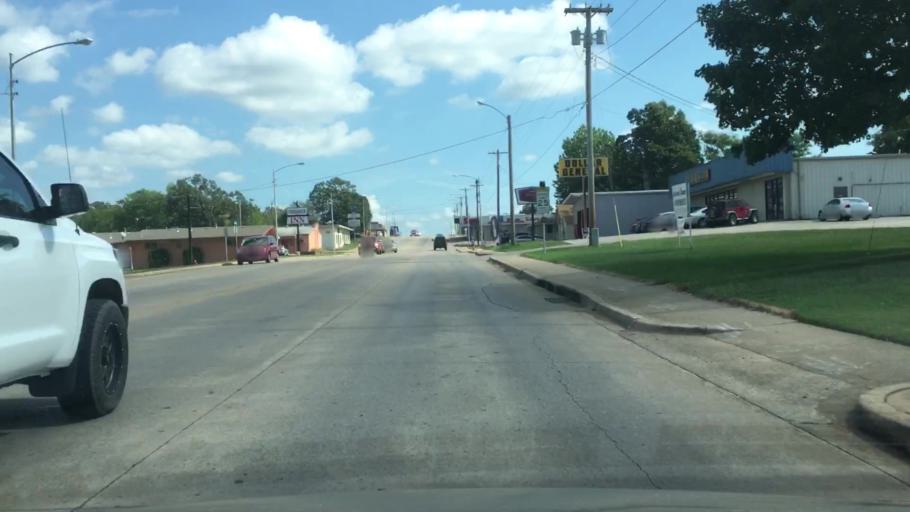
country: US
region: Oklahoma
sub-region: Cherokee County
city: Tahlequah
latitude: 35.9153
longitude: -94.9640
